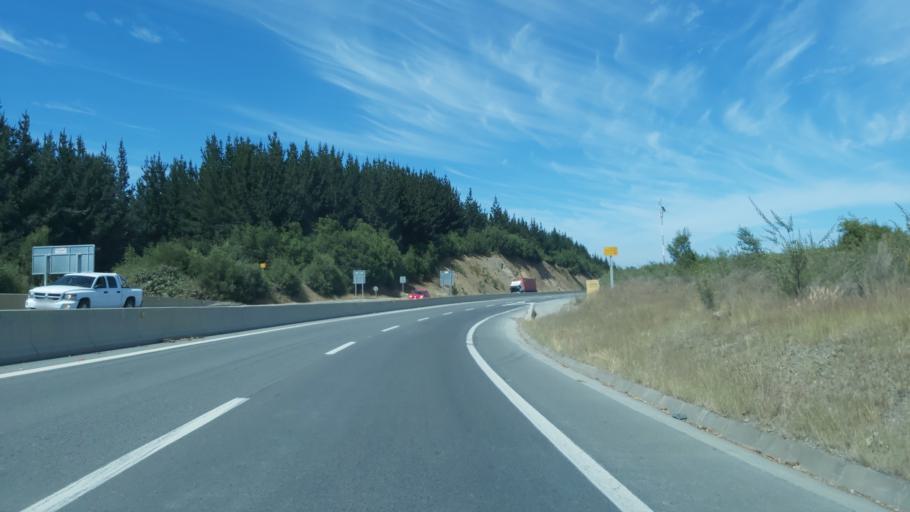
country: CL
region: Biobio
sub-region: Provincia de Concepcion
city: Lota
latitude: -37.0963
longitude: -73.1400
